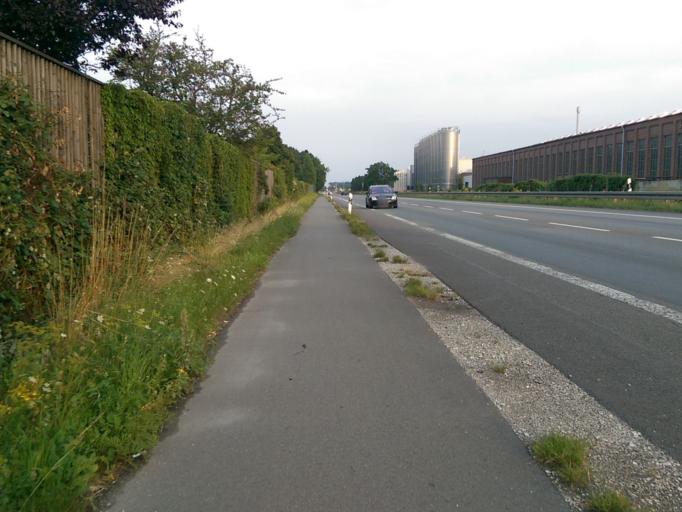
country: DE
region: North Rhine-Westphalia
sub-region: Regierungsbezirk Detmold
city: Rheda-Wiedenbruck
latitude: 51.8775
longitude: 8.2439
